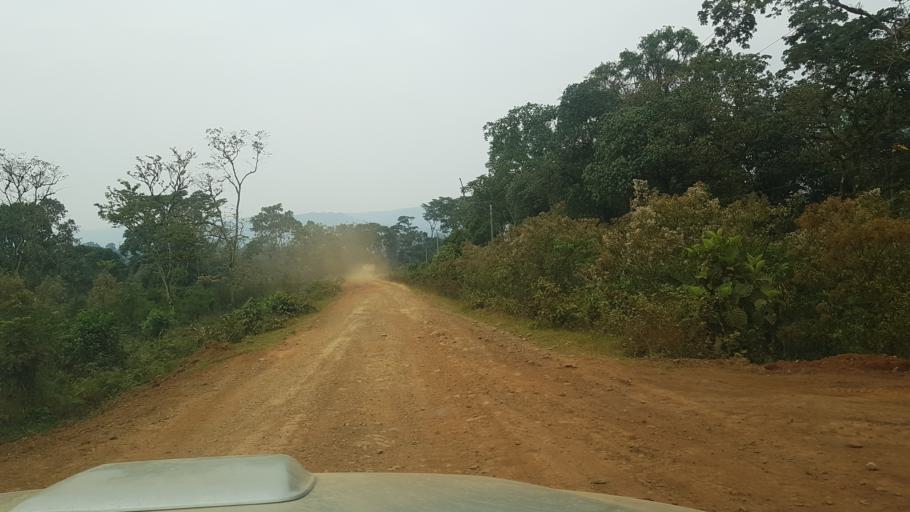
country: ET
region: Oromiya
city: Gore
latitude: 7.8779
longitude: 35.4834
